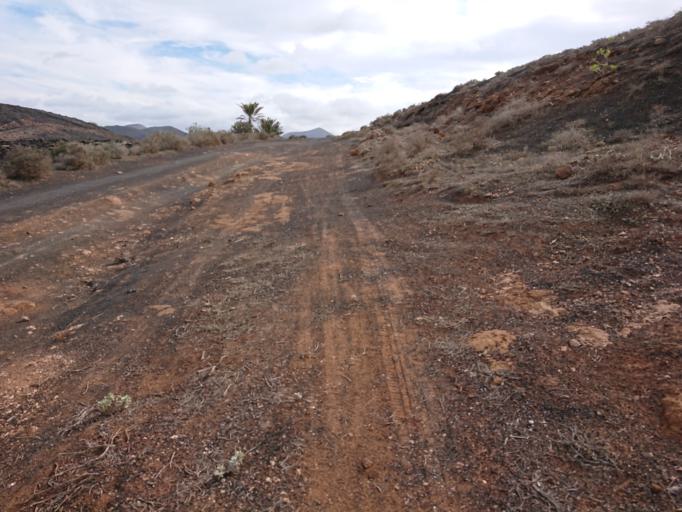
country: ES
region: Canary Islands
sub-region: Provincia de Las Palmas
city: Tinajo
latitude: 29.0192
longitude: -13.6762
